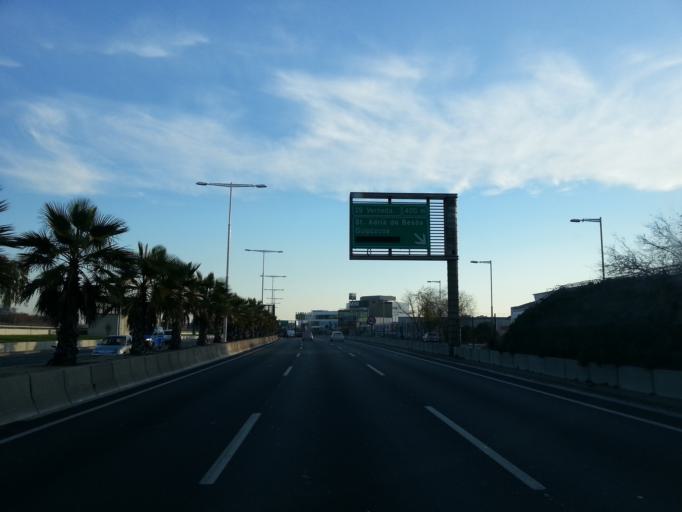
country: ES
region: Catalonia
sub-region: Provincia de Barcelona
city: Sant Adria de Besos
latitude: 41.4354
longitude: 2.2094
